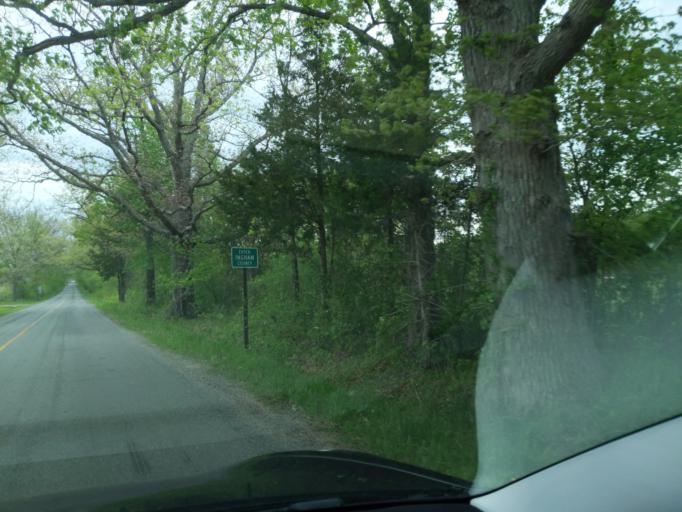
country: US
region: Michigan
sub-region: Ingham County
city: Stockbridge
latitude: 42.4250
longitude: -84.2583
